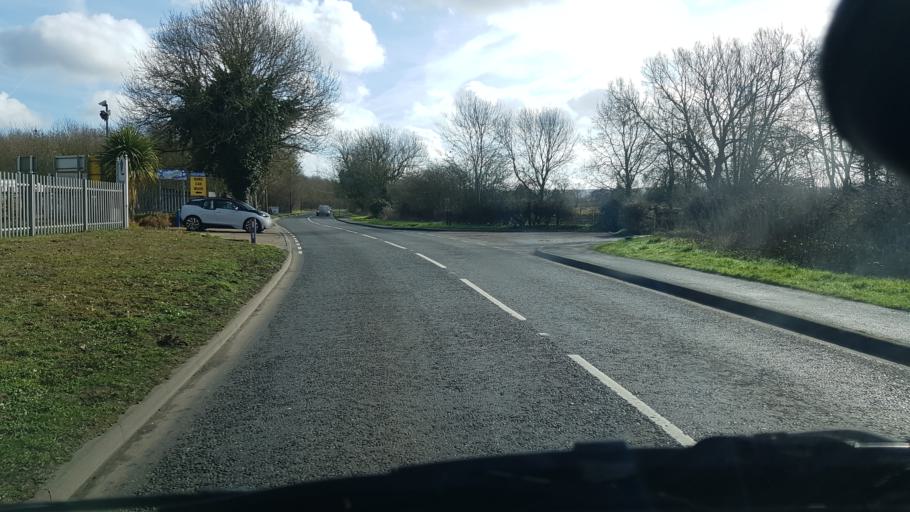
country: GB
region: England
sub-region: Surrey
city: Guildford
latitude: 51.2682
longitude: -0.5588
